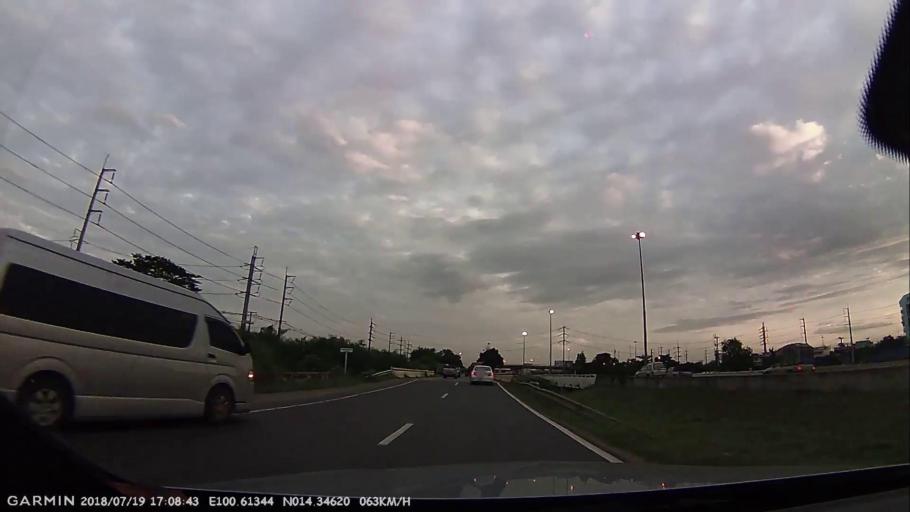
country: TH
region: Phra Nakhon Si Ayutthaya
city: Phra Nakhon Si Ayutthaya
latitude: 14.3461
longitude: 100.6134
